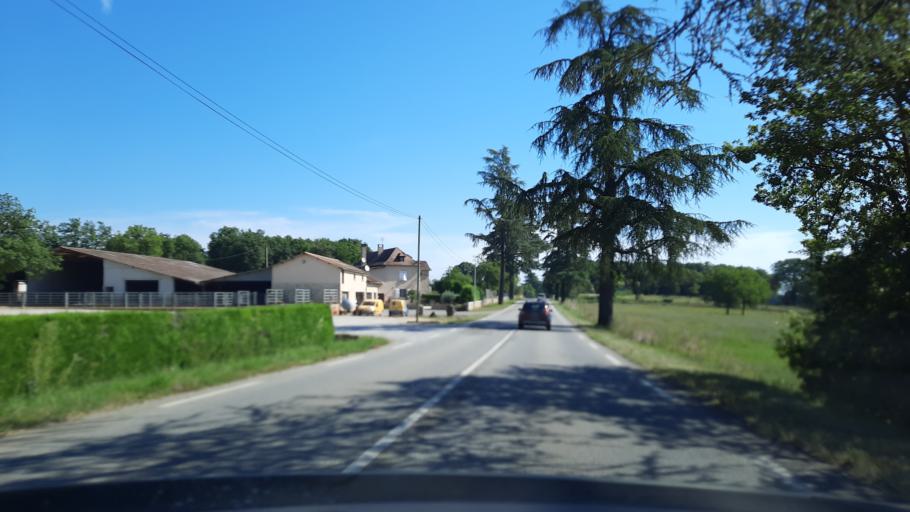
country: FR
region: Midi-Pyrenees
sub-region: Departement du Tarn-et-Garonne
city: Caylus
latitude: 44.2977
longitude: 1.8734
